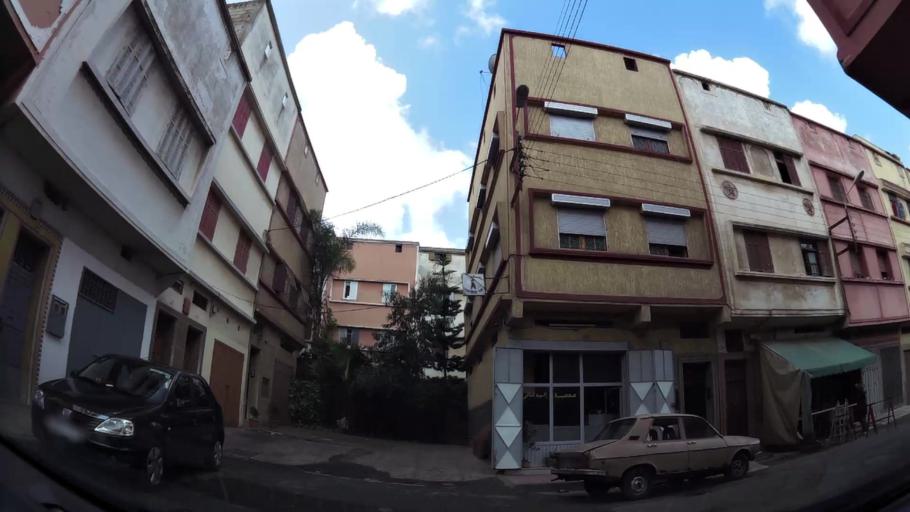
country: MA
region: Grand Casablanca
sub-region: Casablanca
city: Casablanca
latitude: 33.5394
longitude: -7.5874
